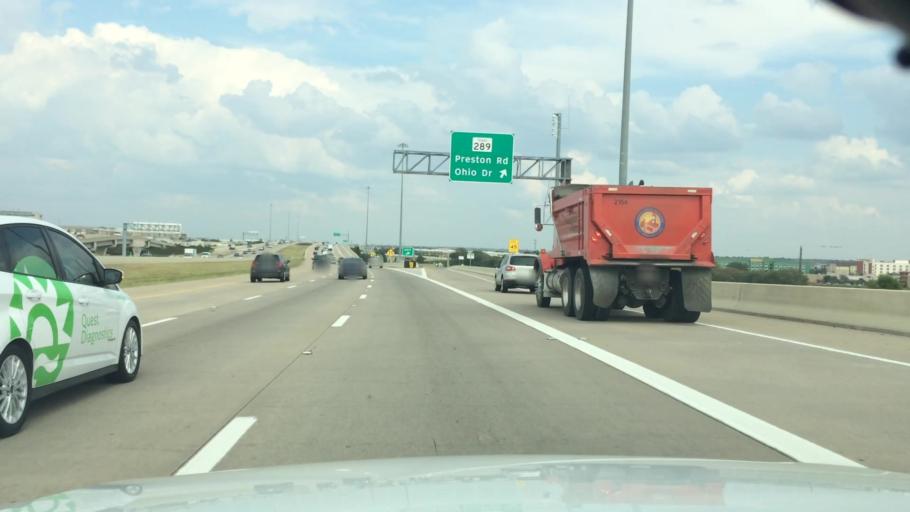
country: US
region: Texas
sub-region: Collin County
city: Frisco
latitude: 33.0937
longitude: -96.8132
